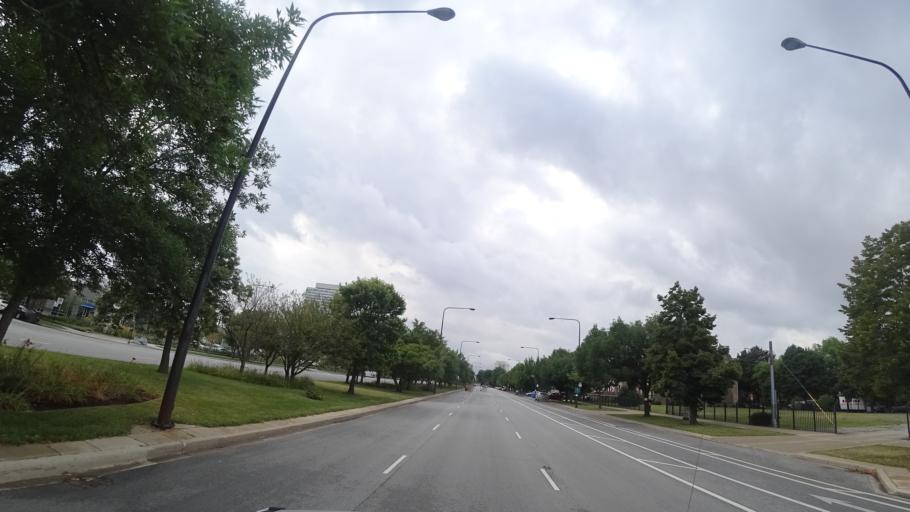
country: US
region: Illinois
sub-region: Cook County
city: Chicago
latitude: 41.8339
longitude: -87.6173
